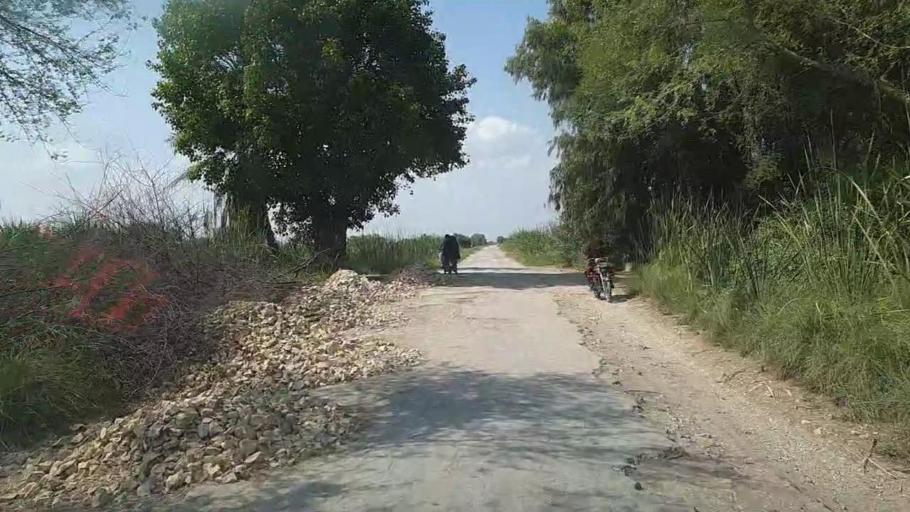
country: PK
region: Sindh
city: Khairpur
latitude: 28.0896
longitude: 69.6316
